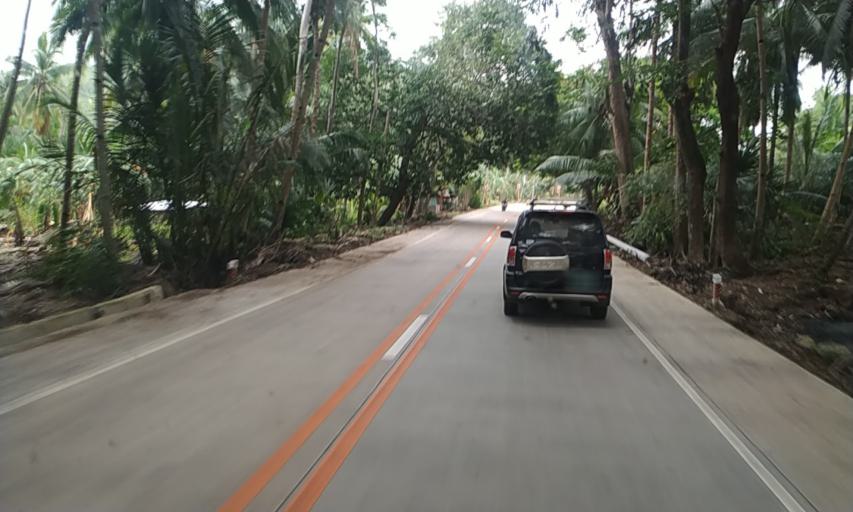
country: PH
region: Central Visayas
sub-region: Province of Negros Oriental
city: Basak
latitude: 10.2089
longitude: 123.3014
